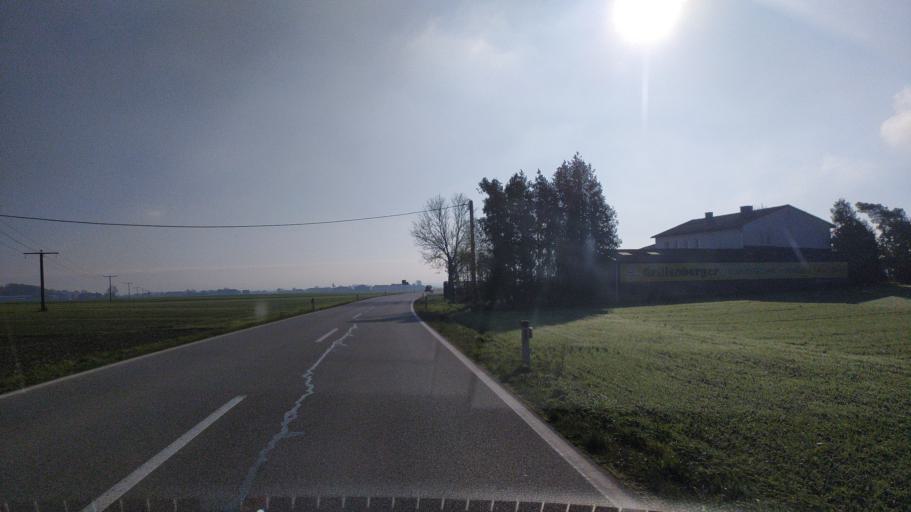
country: AT
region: Upper Austria
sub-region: Politischer Bezirk Perg
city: Perg
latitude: 48.2085
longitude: 14.6530
